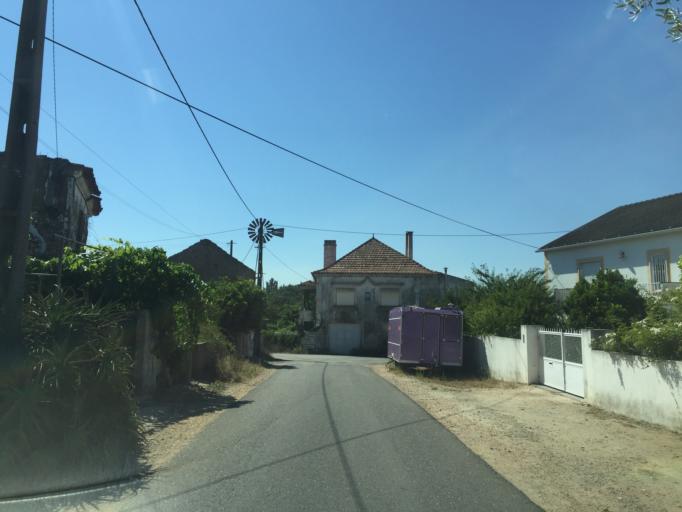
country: PT
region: Santarem
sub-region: Ferreira do Zezere
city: Ferreira do Zezere
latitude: 39.5942
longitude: -8.2919
